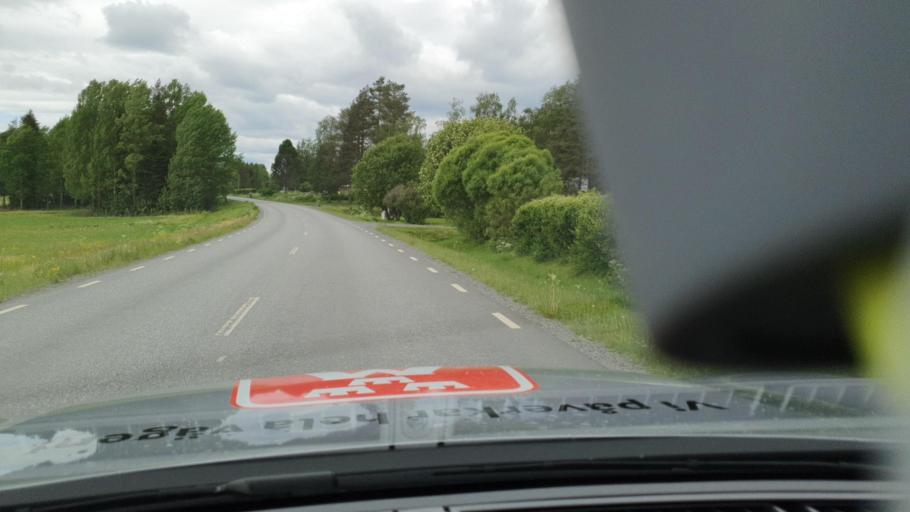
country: SE
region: Norrbotten
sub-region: Lulea Kommun
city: Gammelstad
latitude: 65.8014
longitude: 22.0497
